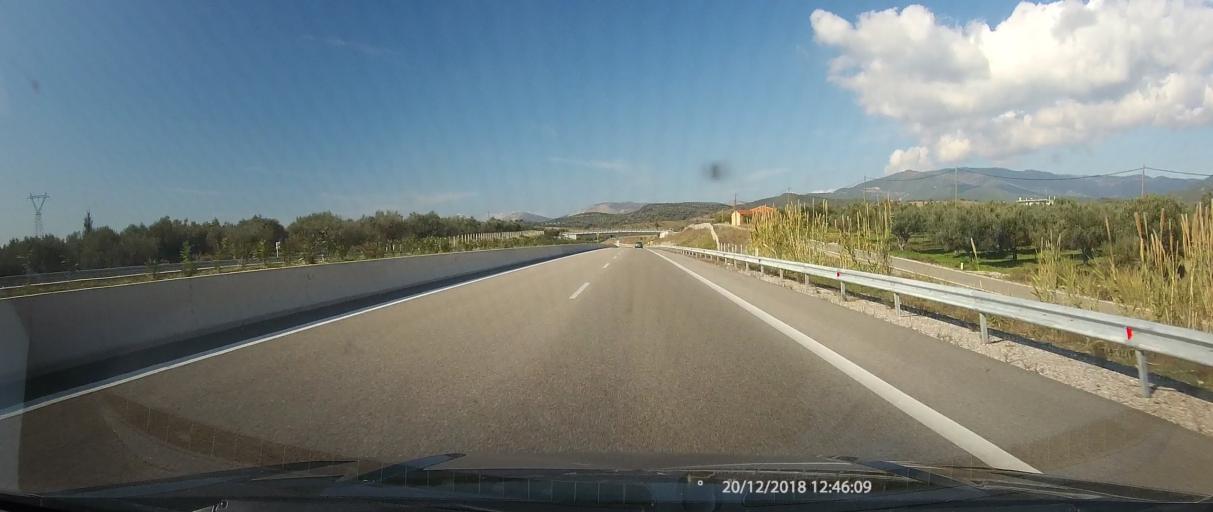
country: GR
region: West Greece
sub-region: Nomos Aitolias kai Akarnanias
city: Mesolongi
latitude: 38.3892
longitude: 21.4796
